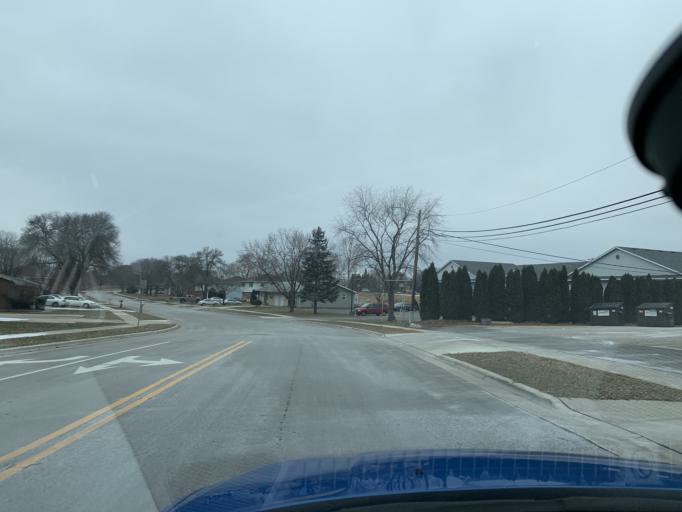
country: US
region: Wisconsin
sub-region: Dane County
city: Sun Prairie
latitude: 43.1956
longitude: -89.2111
